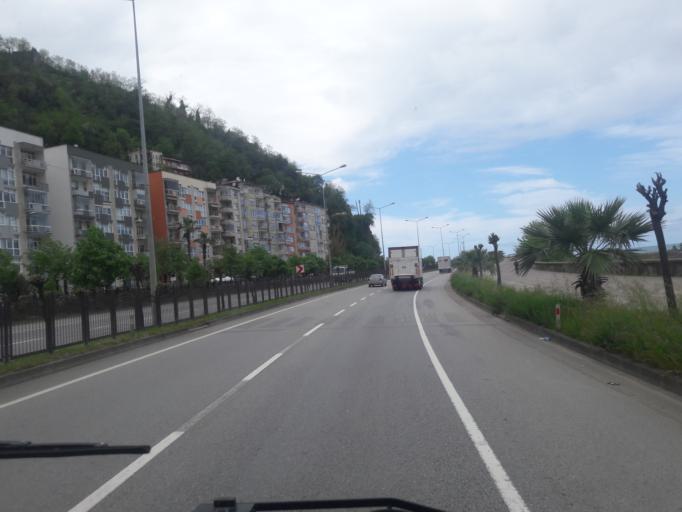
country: TR
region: Giresun
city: Giresun
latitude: 40.9180
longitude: 38.3961
